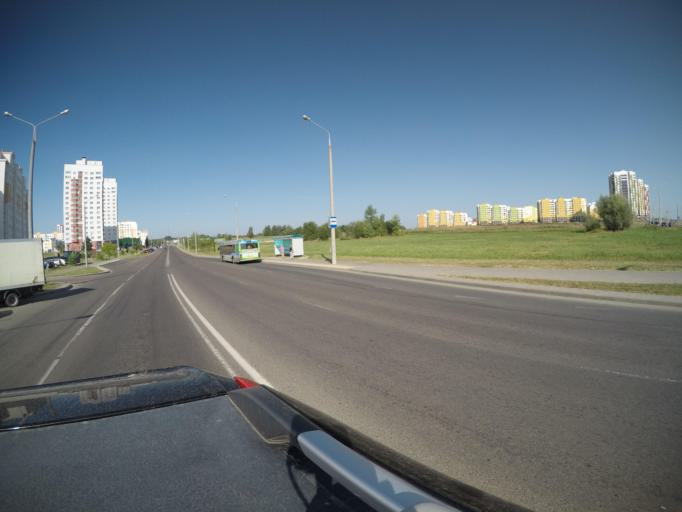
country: BY
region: Grodnenskaya
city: Hrodna
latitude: 53.7135
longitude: 23.8670
